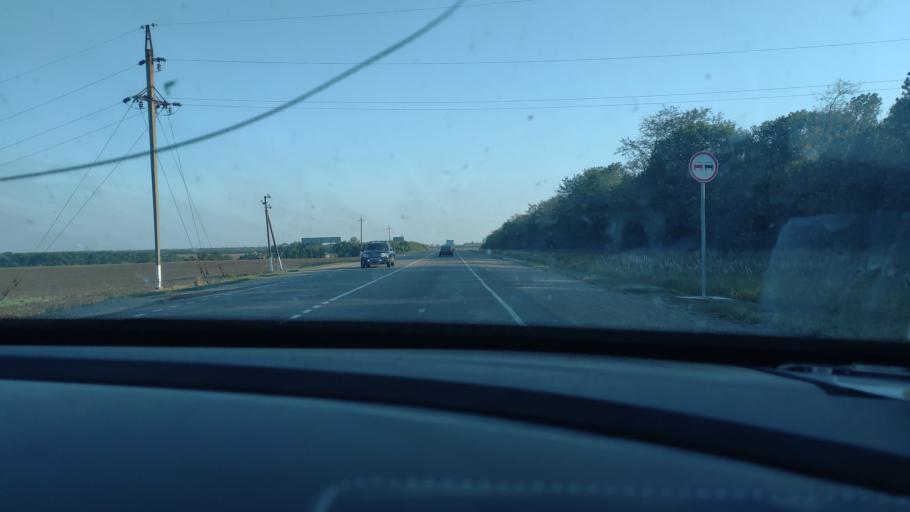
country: RU
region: Krasnodarskiy
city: Novominskaya
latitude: 46.2984
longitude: 38.9330
